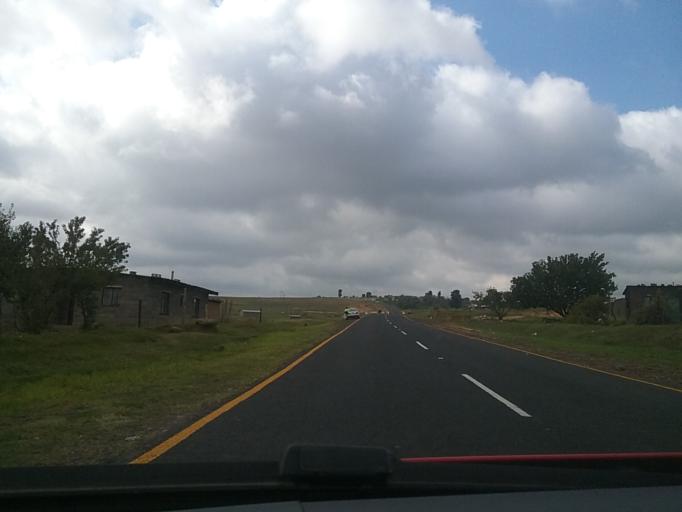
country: LS
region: Berea
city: Teyateyaneng
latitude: -29.1890
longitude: 27.8036
